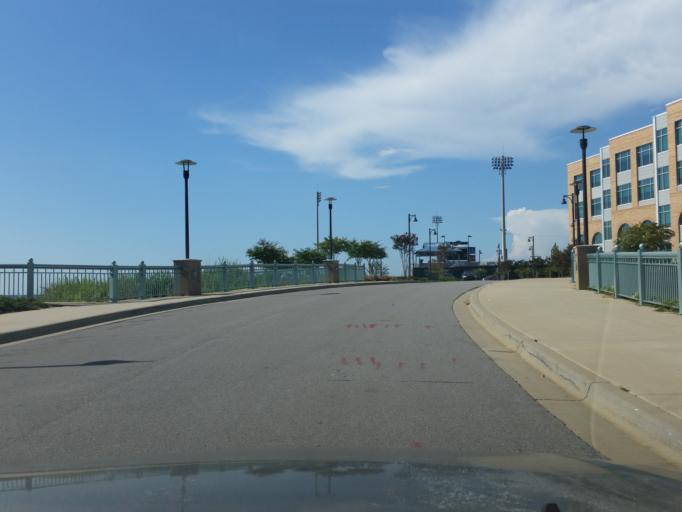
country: US
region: Florida
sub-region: Escambia County
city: Pensacola
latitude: 30.4064
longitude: -87.2176
